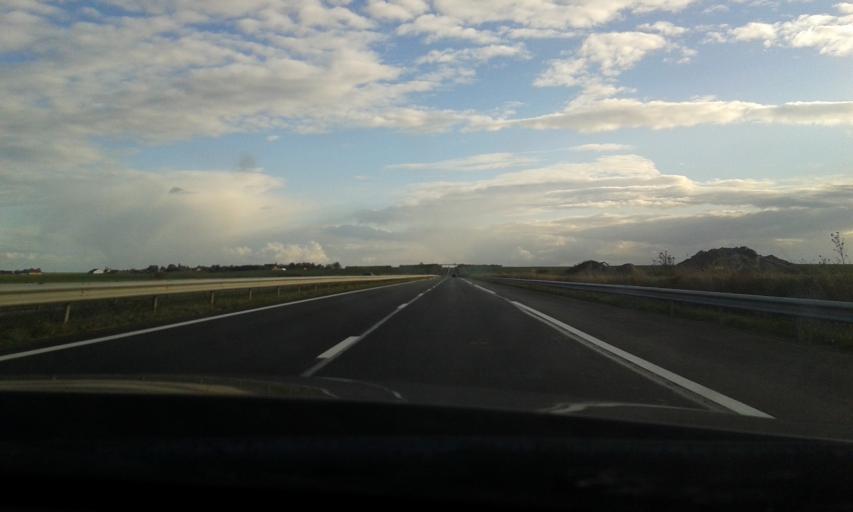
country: FR
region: Centre
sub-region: Departement d'Eure-et-Loir
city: Leves
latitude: 48.5230
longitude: 1.4568
